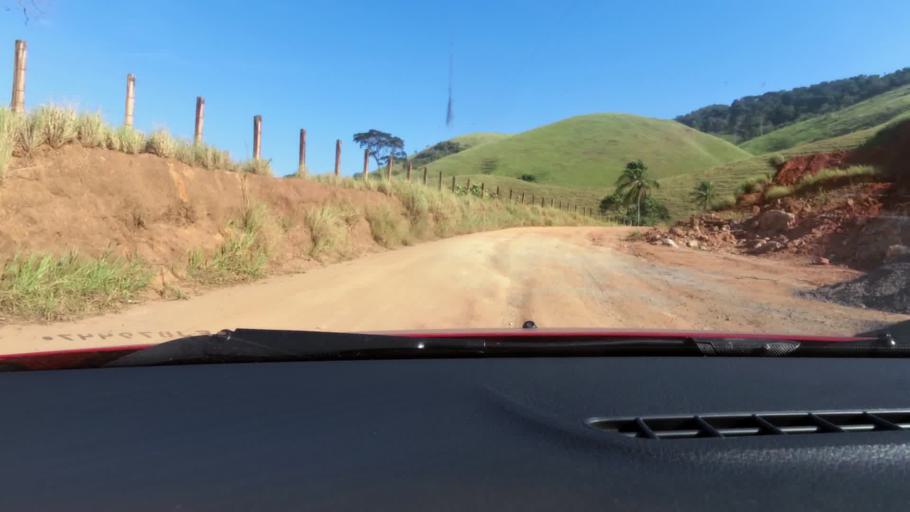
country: BR
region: Espirito Santo
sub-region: Guarapari
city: Guarapari
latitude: -20.5292
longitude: -40.5642
